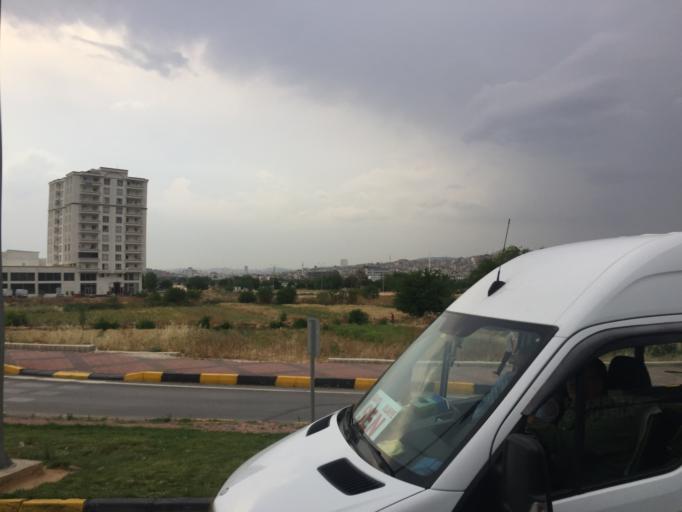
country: TR
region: Gaziantep
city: Gaziantep
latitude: 37.0555
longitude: 37.4155
